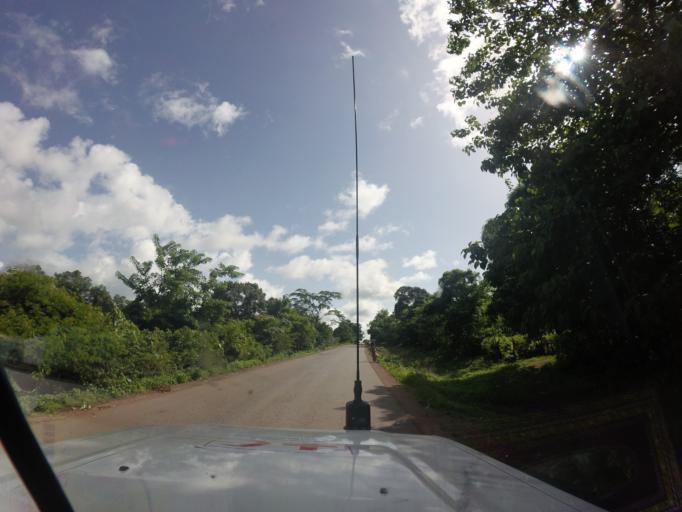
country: GN
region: Mamou
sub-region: Mamou Prefecture
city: Mamou
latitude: 10.3076
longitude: -12.2900
